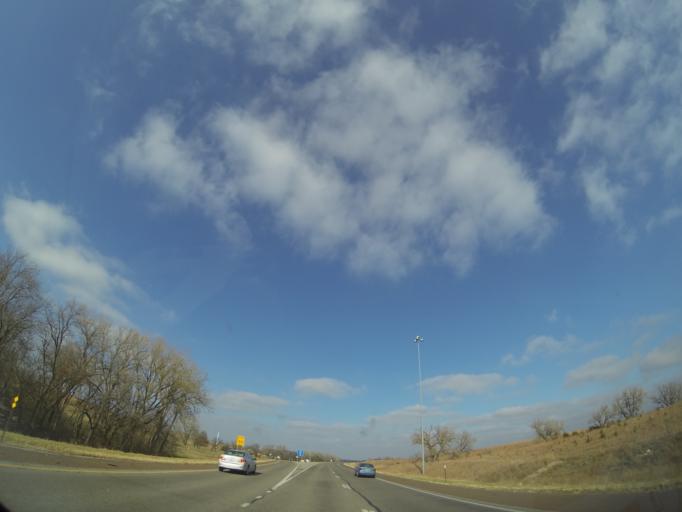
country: US
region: Kansas
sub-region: McPherson County
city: Lindsborg
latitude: 38.4789
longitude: -97.6197
